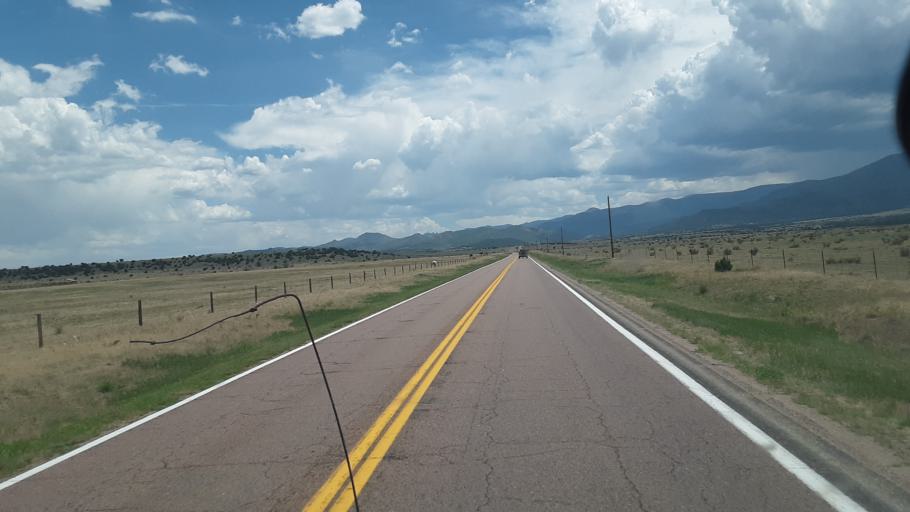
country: US
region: Colorado
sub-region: Fremont County
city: Florence
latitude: 38.2905
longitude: -105.0875
